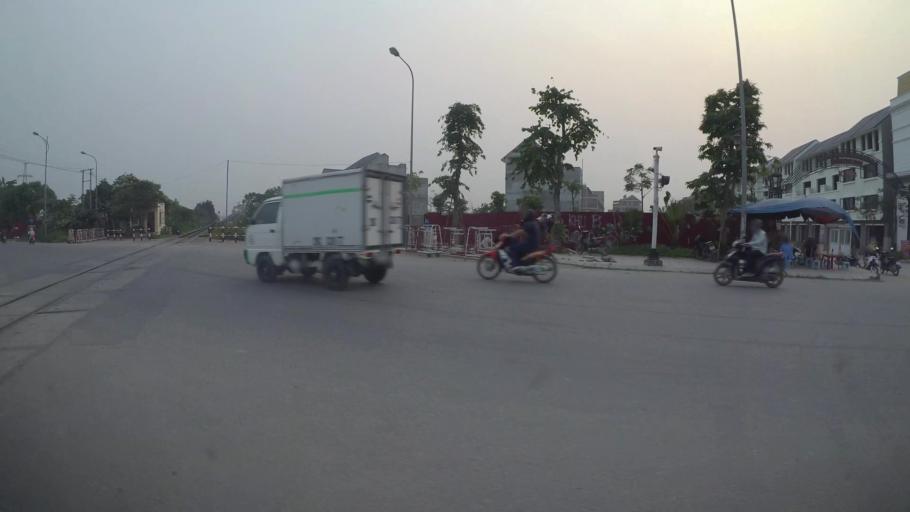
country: VN
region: Ha Noi
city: Ha Dong
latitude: 20.9961
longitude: 105.7350
